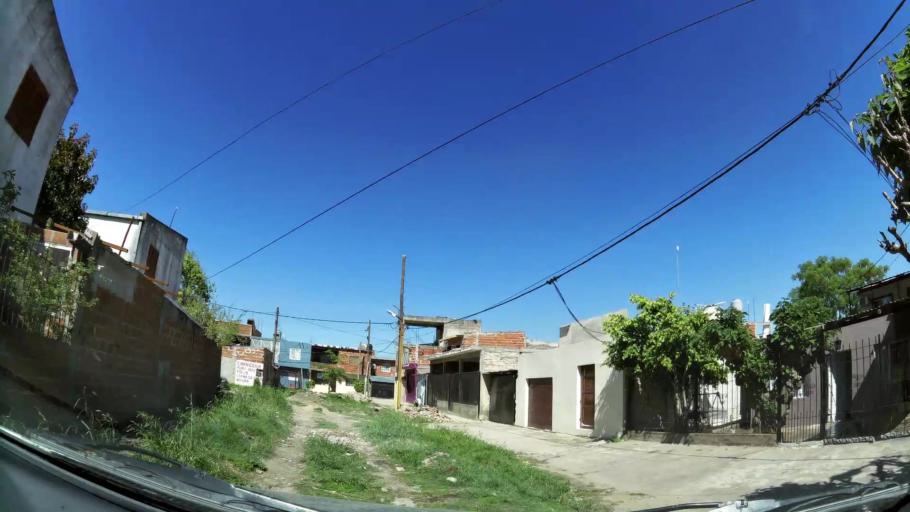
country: AR
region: Buenos Aires
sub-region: Partido de Quilmes
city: Quilmes
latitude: -34.7056
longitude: -58.3010
